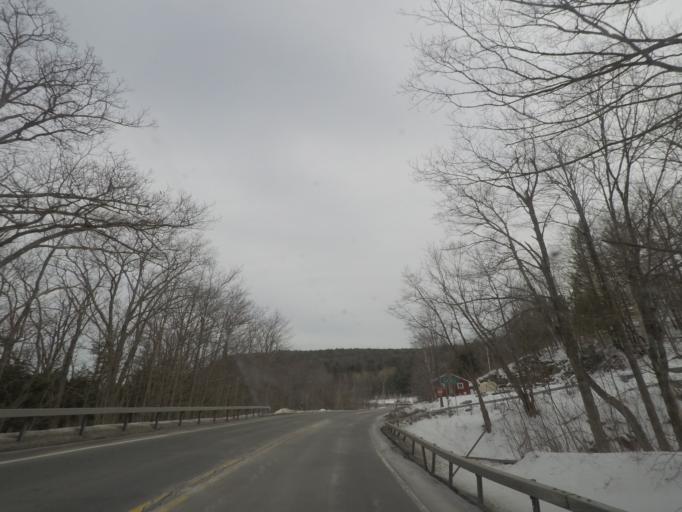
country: US
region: New York
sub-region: Albany County
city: Voorheesville
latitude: 42.5960
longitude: -74.0094
